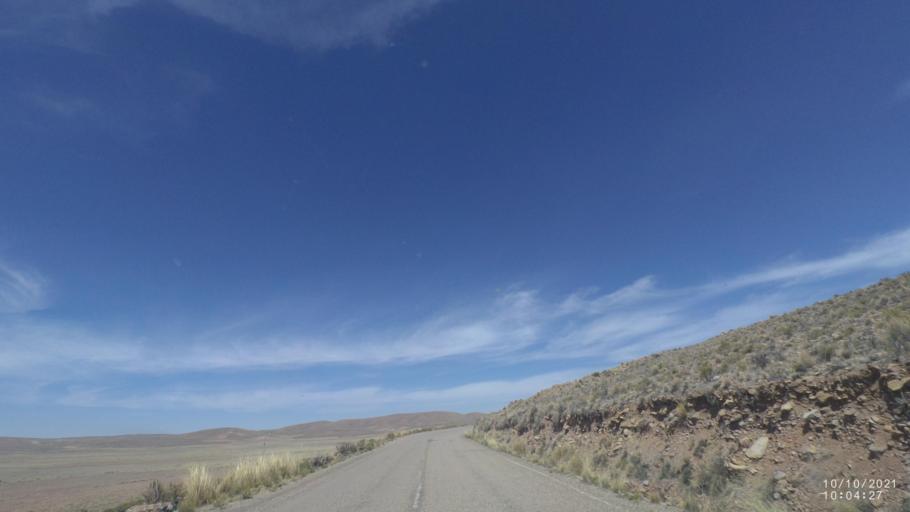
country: BO
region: La Paz
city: Eucaliptus
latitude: -17.3821
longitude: -67.4463
